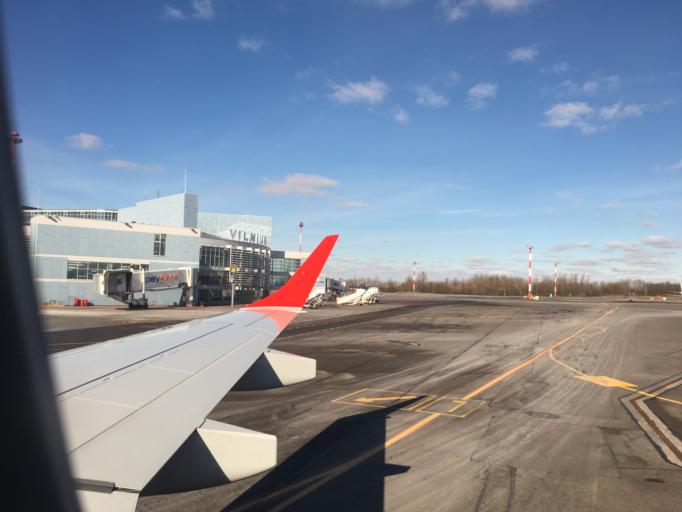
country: LT
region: Vilnius County
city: Naujamiestis
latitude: 54.6420
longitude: 25.2836
